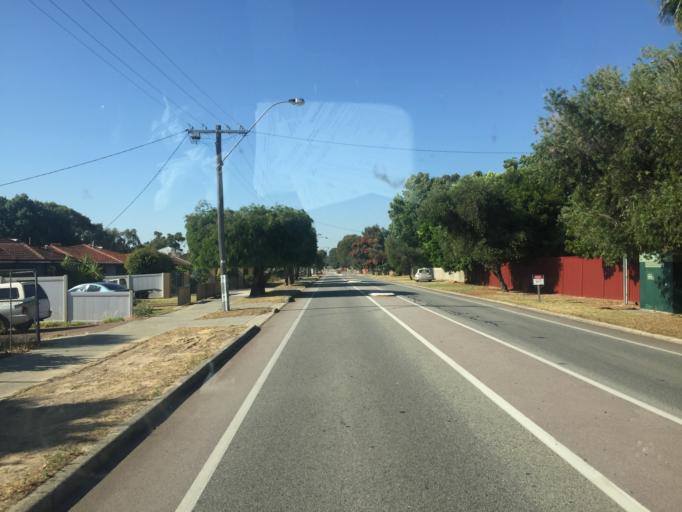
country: AU
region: Western Australia
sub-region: Gosnells
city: Maddington
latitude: -32.0360
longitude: 115.9821
